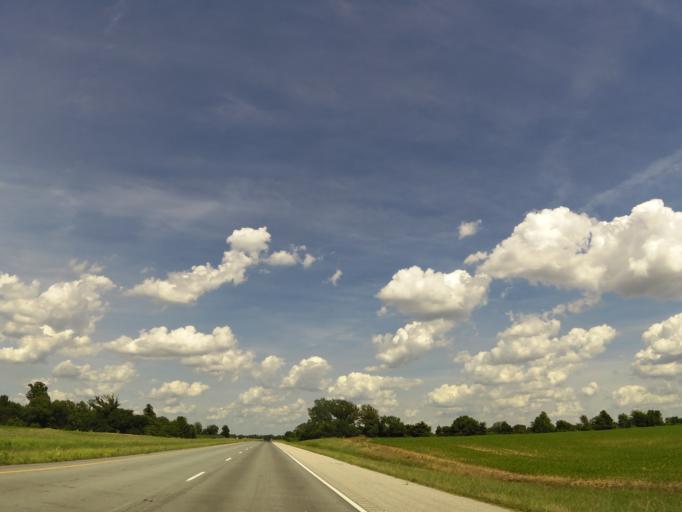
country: US
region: Tennessee
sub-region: Gibson County
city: Dyer
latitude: 35.9944
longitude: -89.0218
